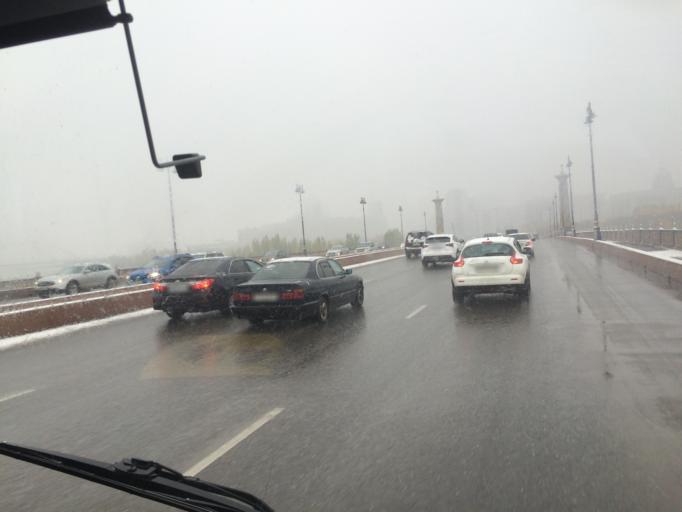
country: KZ
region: Astana Qalasy
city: Astana
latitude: 51.1381
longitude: 71.4433
